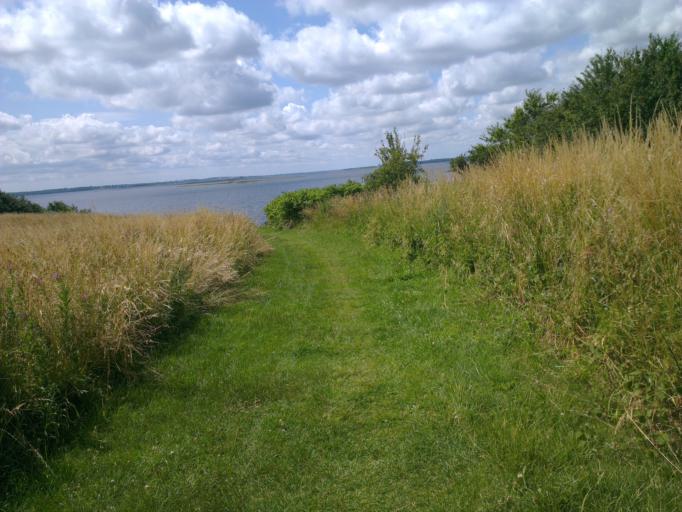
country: DK
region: Zealand
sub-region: Lejre Kommune
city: Ejby
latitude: 55.7502
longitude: 11.8584
